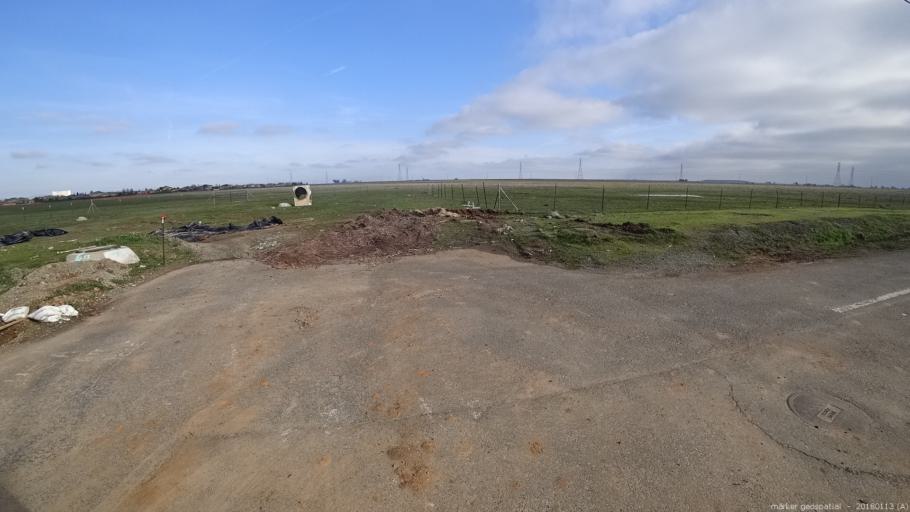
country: US
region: California
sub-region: Sacramento County
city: Gold River
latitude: 38.5500
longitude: -121.2243
